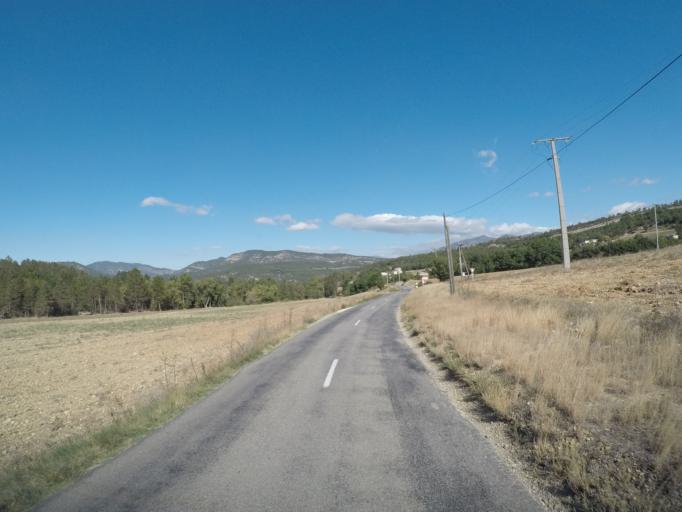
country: FR
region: Provence-Alpes-Cote d'Azur
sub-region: Departement des Alpes-de-Haute-Provence
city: Mallemoisson
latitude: 44.0406
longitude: 6.1684
